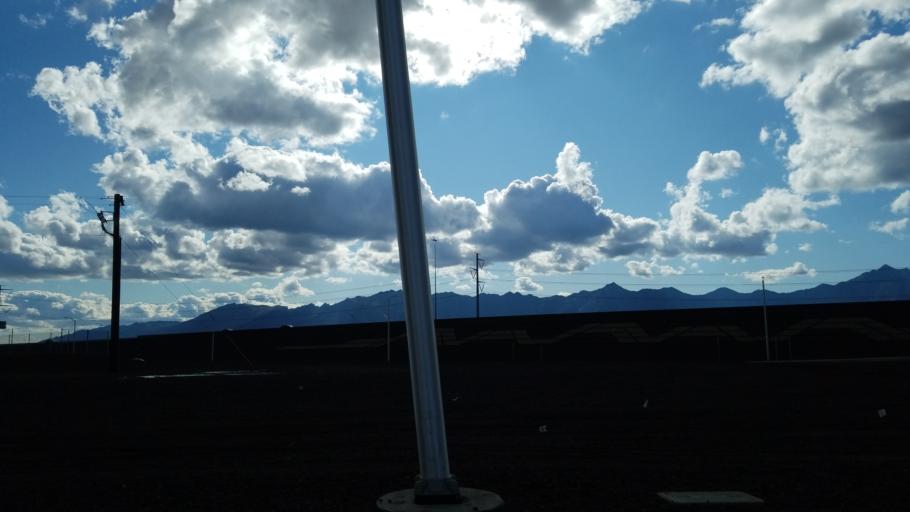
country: US
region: Arizona
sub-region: Maricopa County
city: Laveen
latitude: 33.3343
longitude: -112.1744
